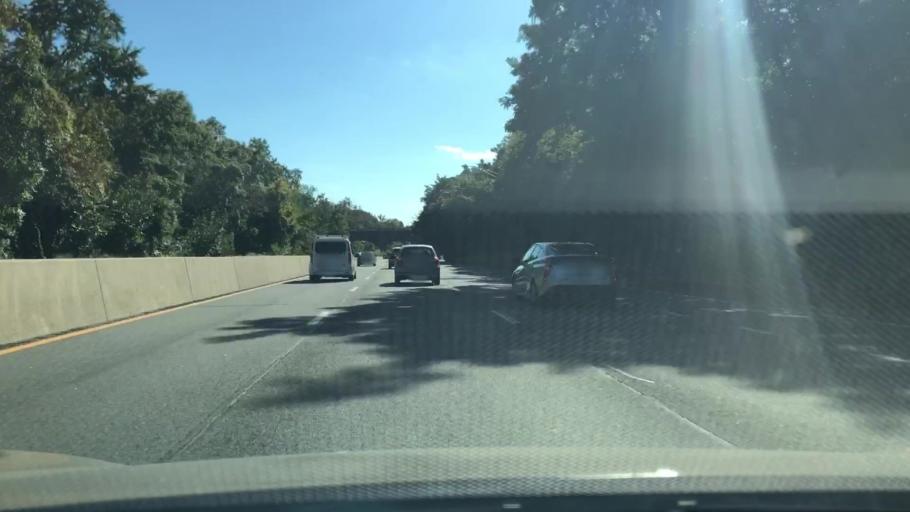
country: US
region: New York
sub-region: Westchester County
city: Yonkers
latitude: 40.9141
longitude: -73.8841
